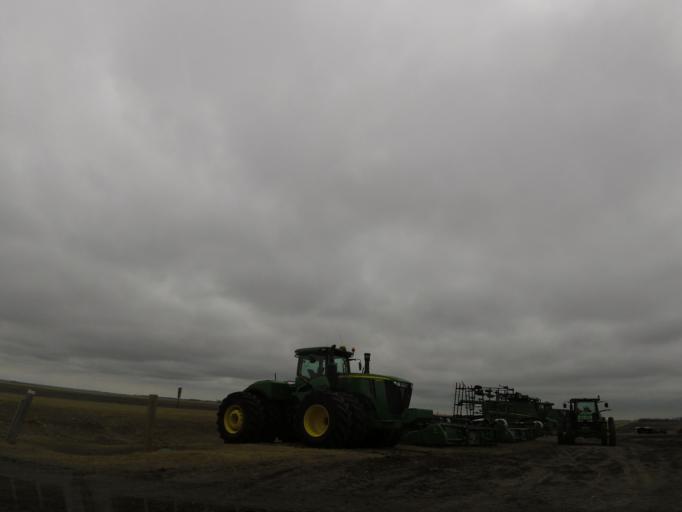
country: US
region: North Dakota
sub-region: Traill County
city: Hillsboro
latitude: 47.1949
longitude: -97.2162
